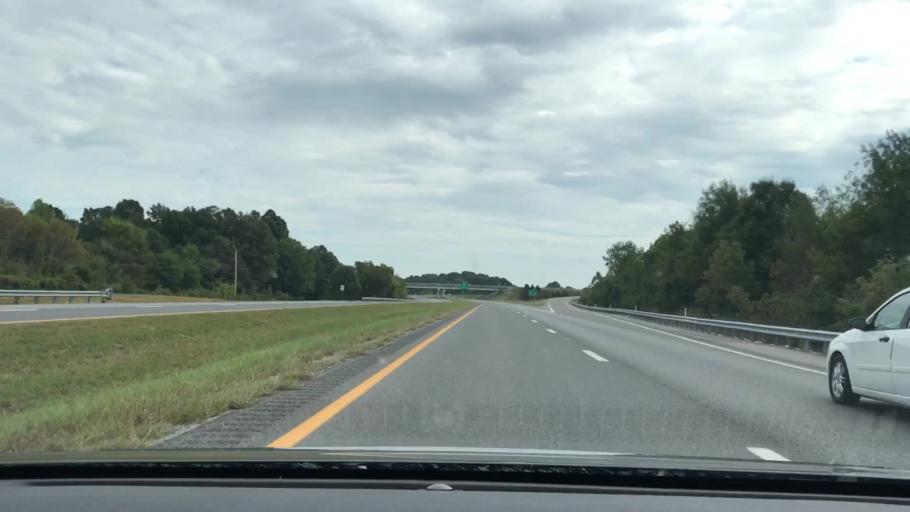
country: US
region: Kentucky
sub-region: Marshall County
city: Benton
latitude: 36.8477
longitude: -88.3847
